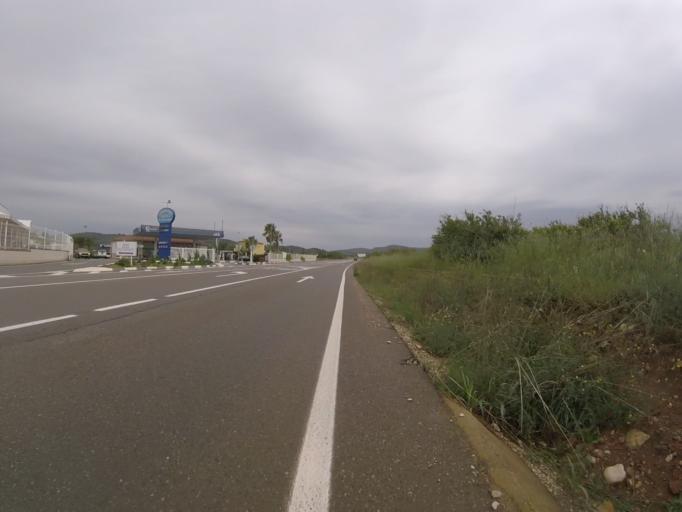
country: ES
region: Valencia
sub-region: Provincia de Castello
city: Alcoceber
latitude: 40.2560
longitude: 0.2451
